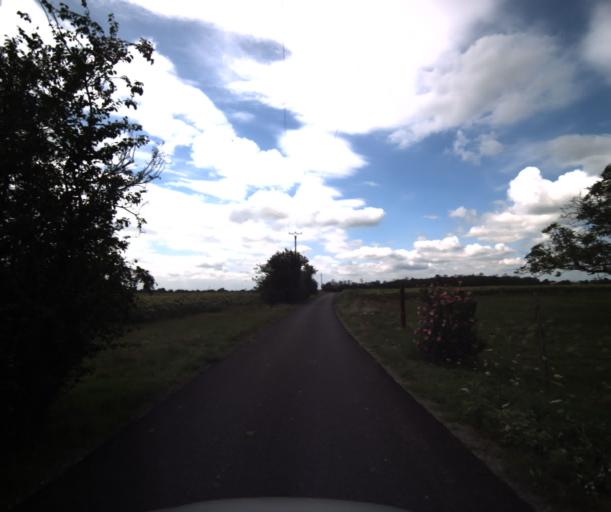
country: FR
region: Midi-Pyrenees
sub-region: Departement de la Haute-Garonne
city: Longages
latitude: 43.3765
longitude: 1.2505
